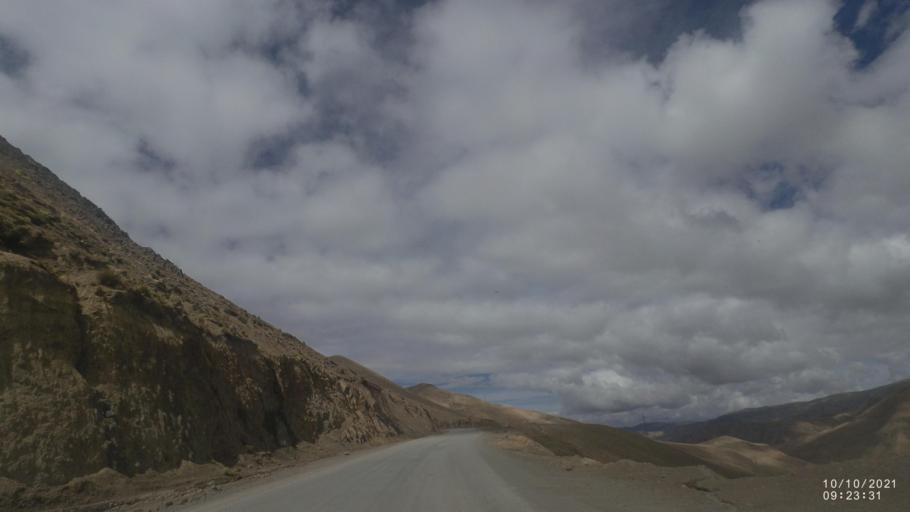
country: BO
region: La Paz
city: Quime
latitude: -17.0854
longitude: -67.3033
